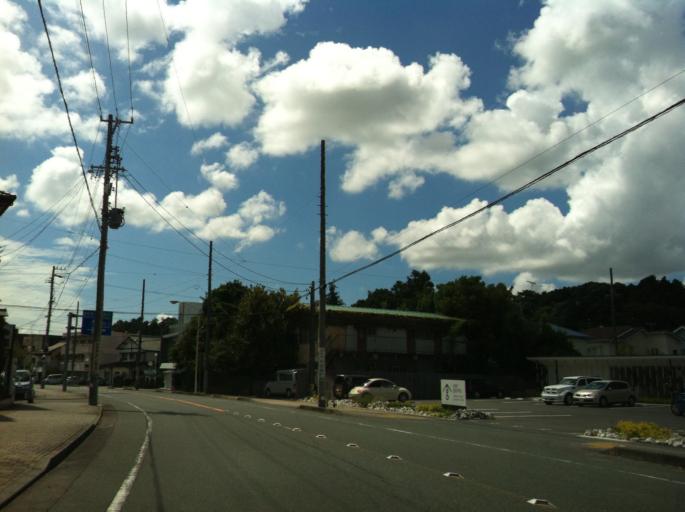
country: JP
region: Shizuoka
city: Kakegawa
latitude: 34.7604
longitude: 138.0842
